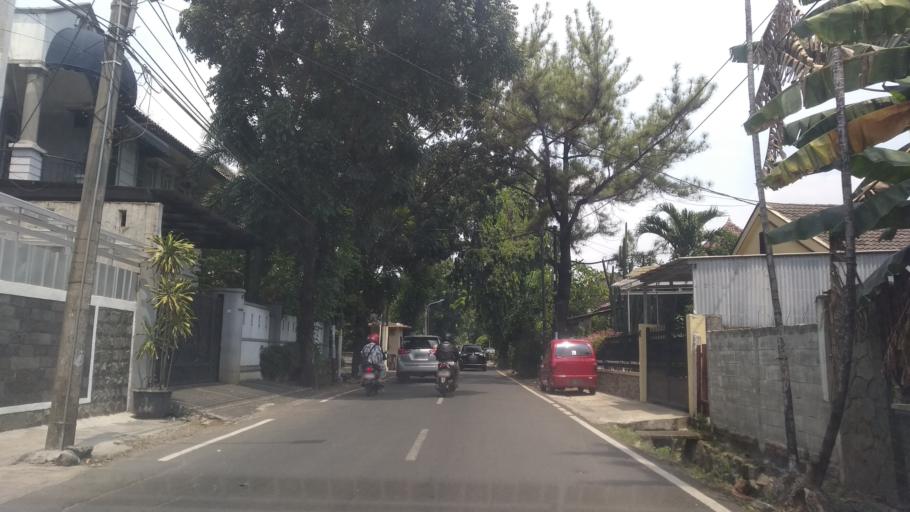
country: ID
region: Banten
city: South Tangerang
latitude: -6.2498
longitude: 106.7746
